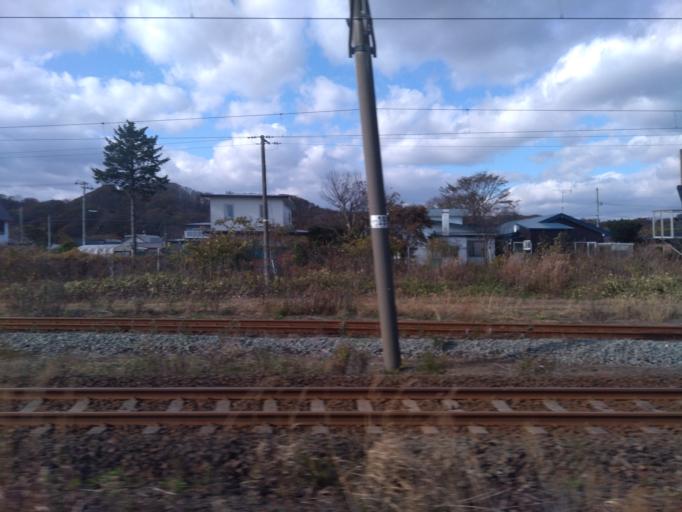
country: JP
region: Hokkaido
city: Shiraoi
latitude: 42.4953
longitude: 141.2640
